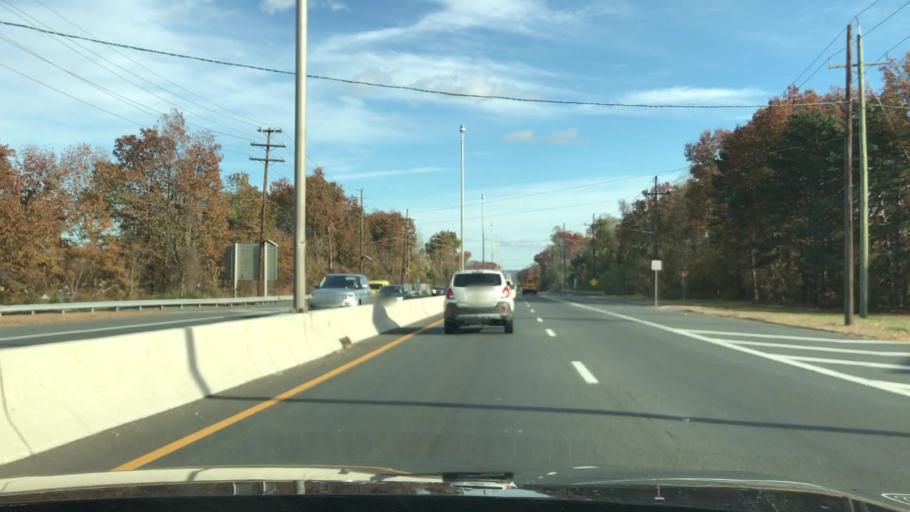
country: US
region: New Jersey
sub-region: Bergen County
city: Fair Lawn
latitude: 40.9336
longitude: -74.1182
